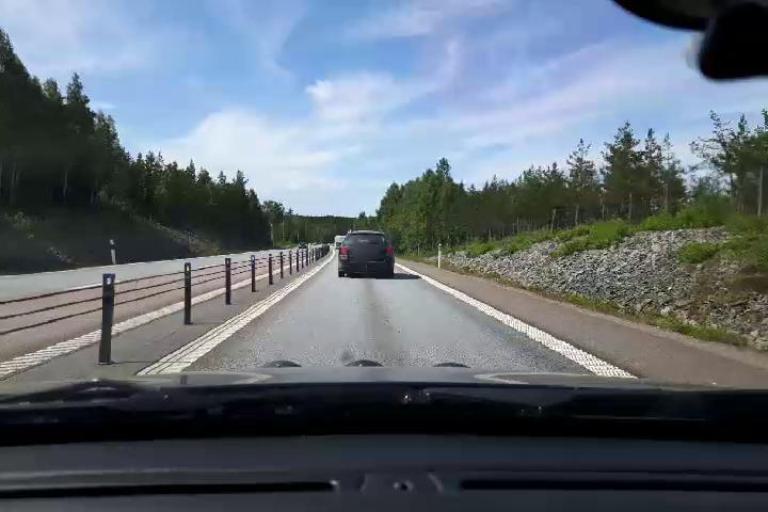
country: SE
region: Gaevleborg
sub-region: Gavle Kommun
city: Norrsundet
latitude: 60.8969
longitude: 17.0267
